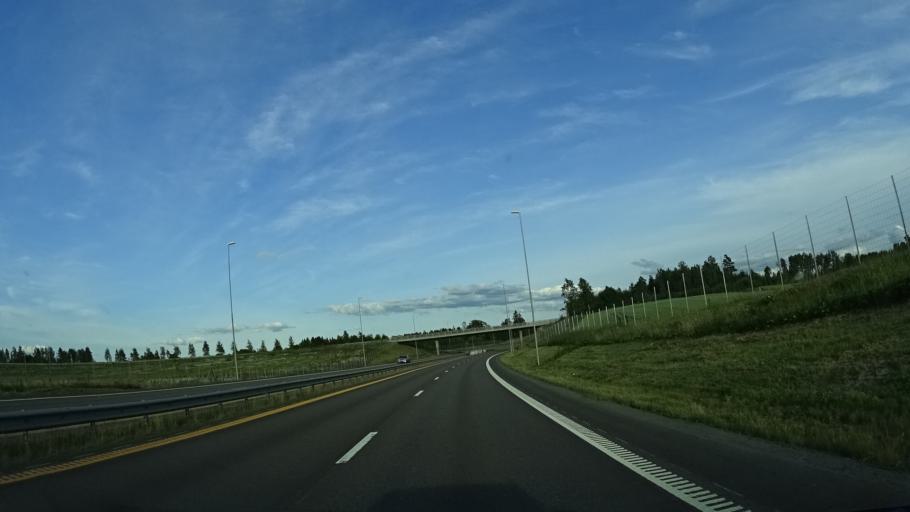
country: NO
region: Ostfold
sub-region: Hobol
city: Knappstad
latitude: 59.6056
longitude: 11.0471
